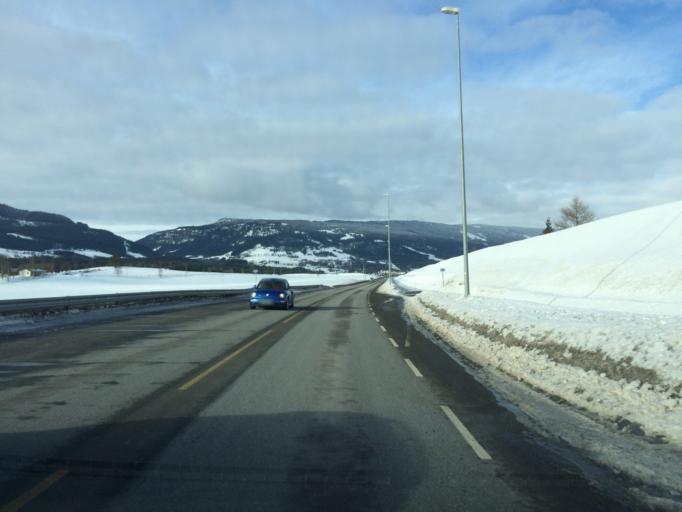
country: NO
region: Oppland
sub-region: Gausdal
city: Segalstad bru
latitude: 61.2200
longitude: 10.2522
